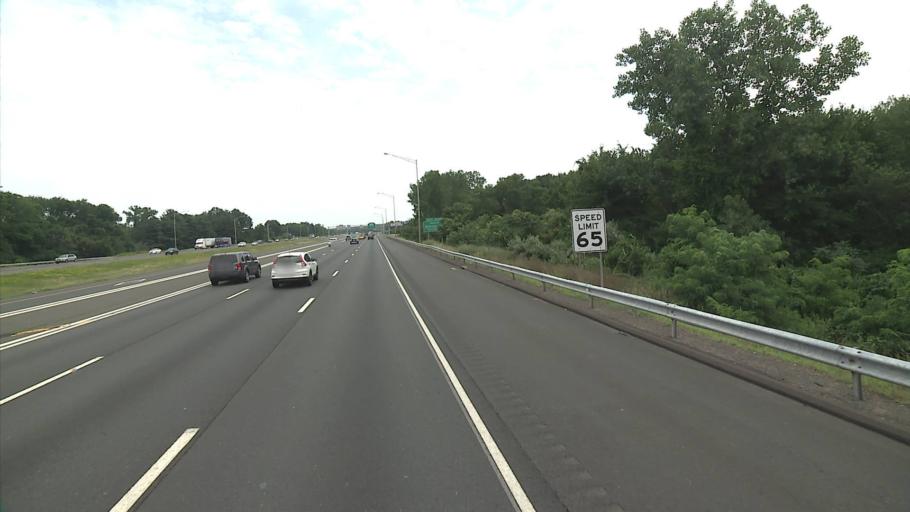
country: US
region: Connecticut
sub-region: Hartford County
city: Manchester
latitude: 41.8167
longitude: -72.5103
